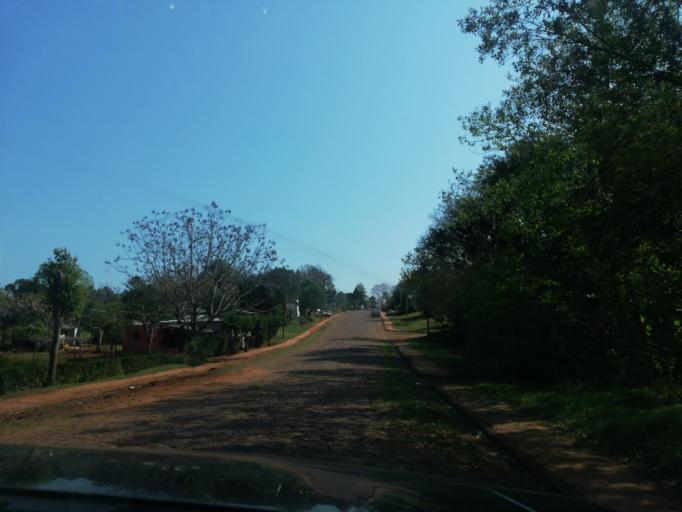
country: AR
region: Misiones
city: Bonpland
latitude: -27.4824
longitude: -55.4814
